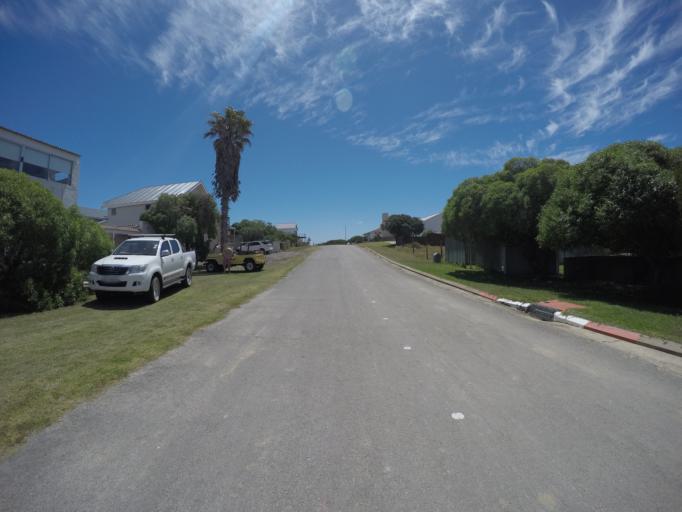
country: ZA
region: Western Cape
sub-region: Eden District Municipality
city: Riversdale
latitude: -34.4209
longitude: 20.8545
